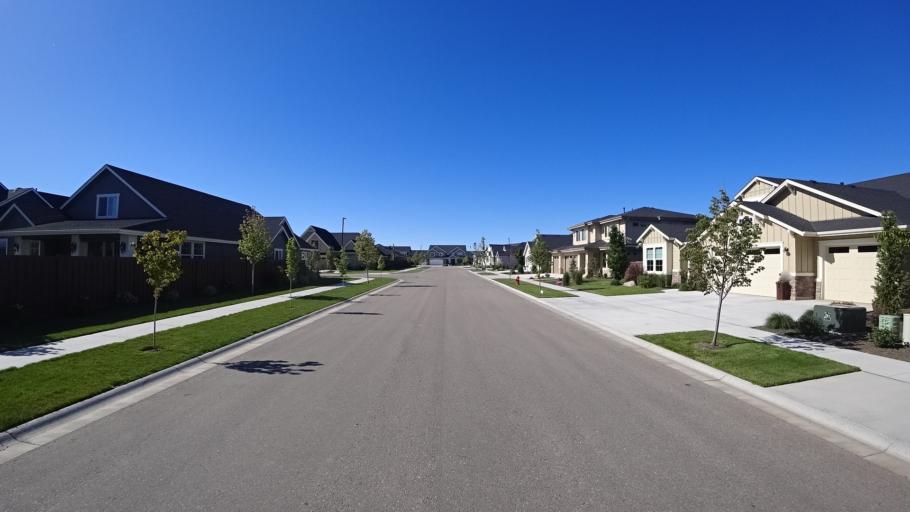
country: US
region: Idaho
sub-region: Ada County
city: Star
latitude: 43.6582
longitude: -116.4420
